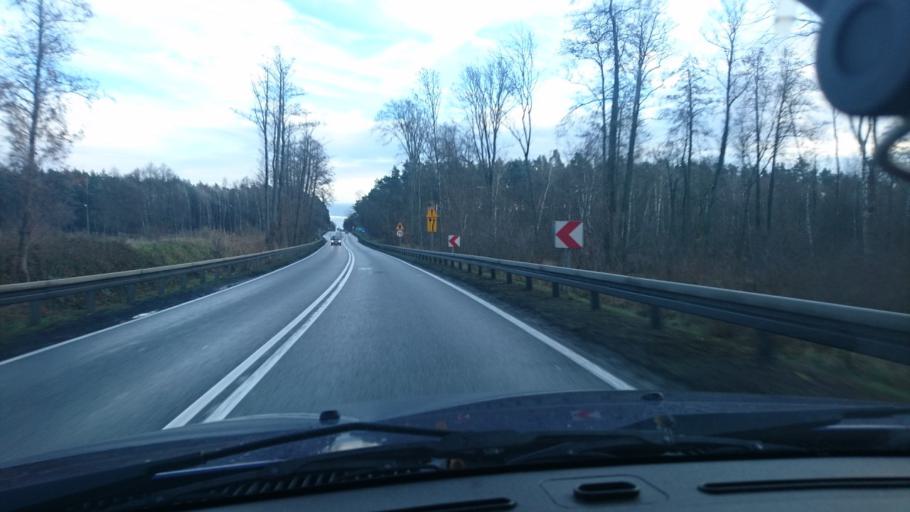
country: PL
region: Greater Poland Voivodeship
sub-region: Powiat kepinski
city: Kepno
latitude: 51.3279
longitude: 17.9615
